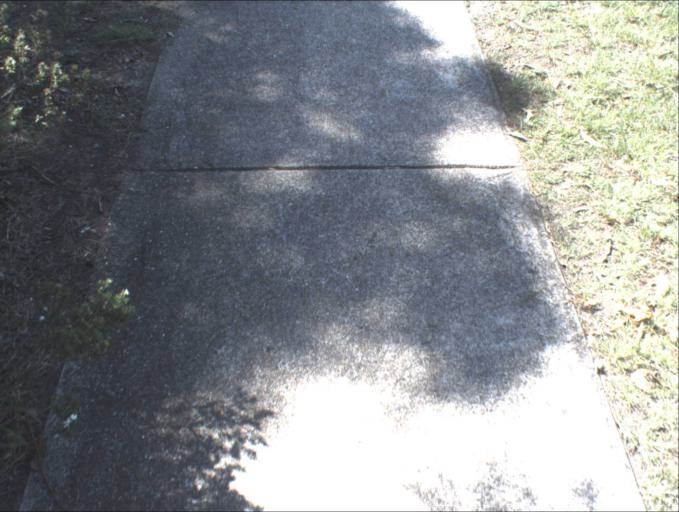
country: AU
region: Queensland
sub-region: Logan
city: Beenleigh
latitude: -27.7032
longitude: 153.1734
